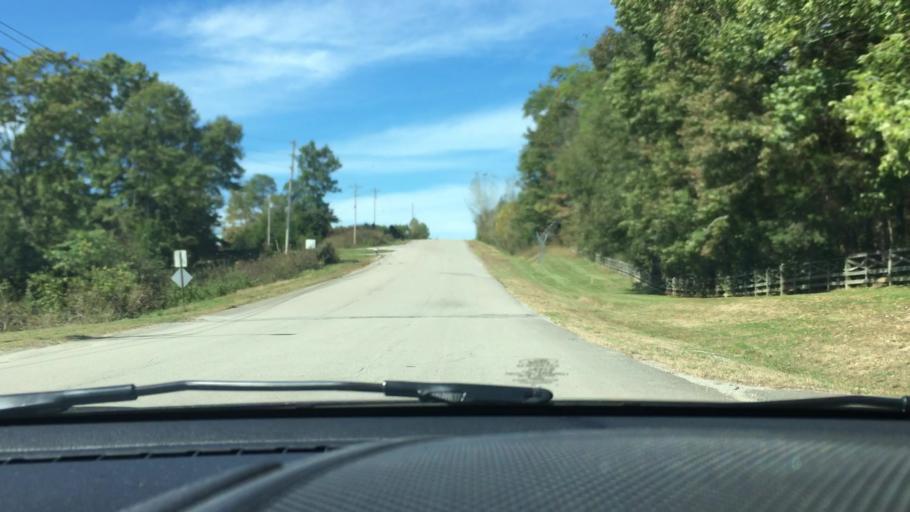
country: US
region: Tennessee
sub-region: Giles County
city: Pulaski
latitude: 35.2218
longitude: -87.0656
